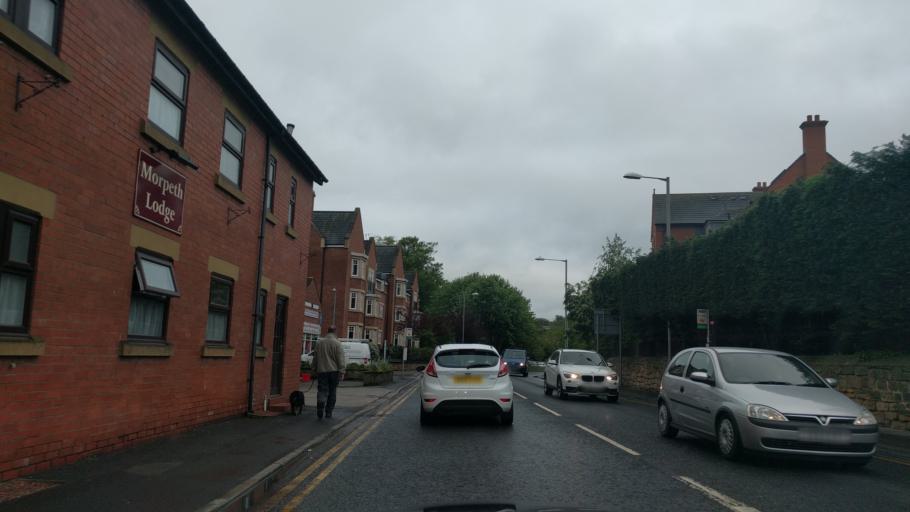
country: GB
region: England
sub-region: Northumberland
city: Morpeth
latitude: 55.1682
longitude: -1.6856
